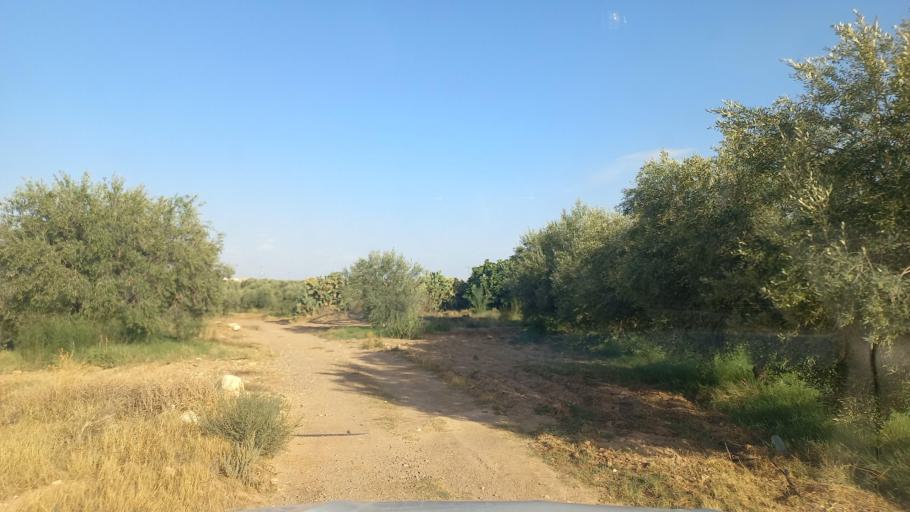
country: TN
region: Al Qasrayn
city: Kasserine
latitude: 35.2682
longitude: 9.0313
